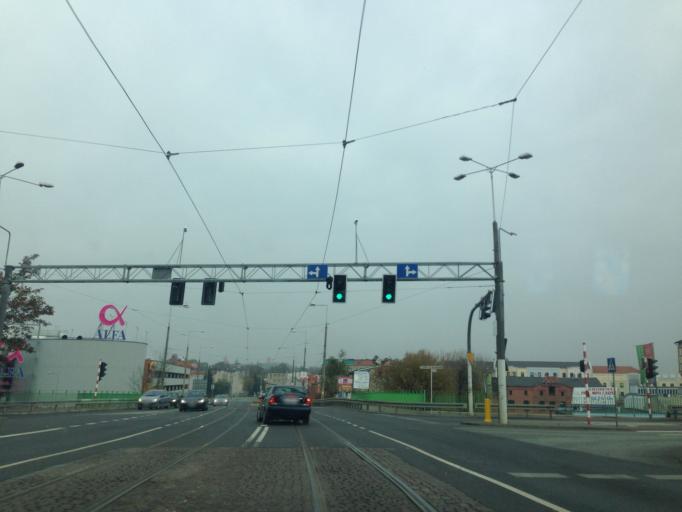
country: PL
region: Kujawsko-Pomorskie
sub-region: Grudziadz
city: Grudziadz
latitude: 53.4823
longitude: 18.7488
